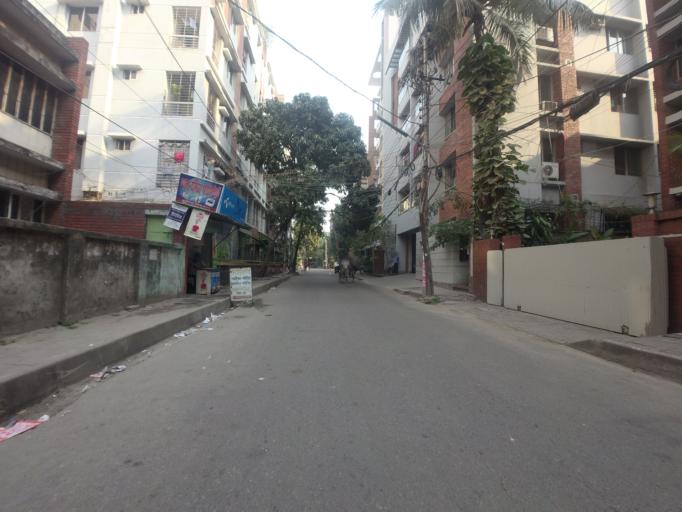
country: BD
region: Dhaka
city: Azimpur
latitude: 23.7623
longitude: 90.3696
